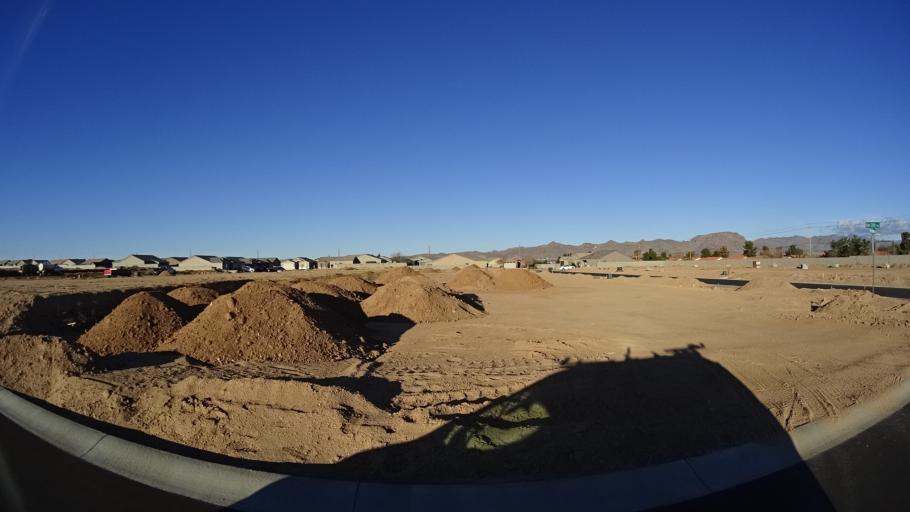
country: US
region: Arizona
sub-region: Mohave County
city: New Kingman-Butler
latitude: 35.2241
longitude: -113.9896
